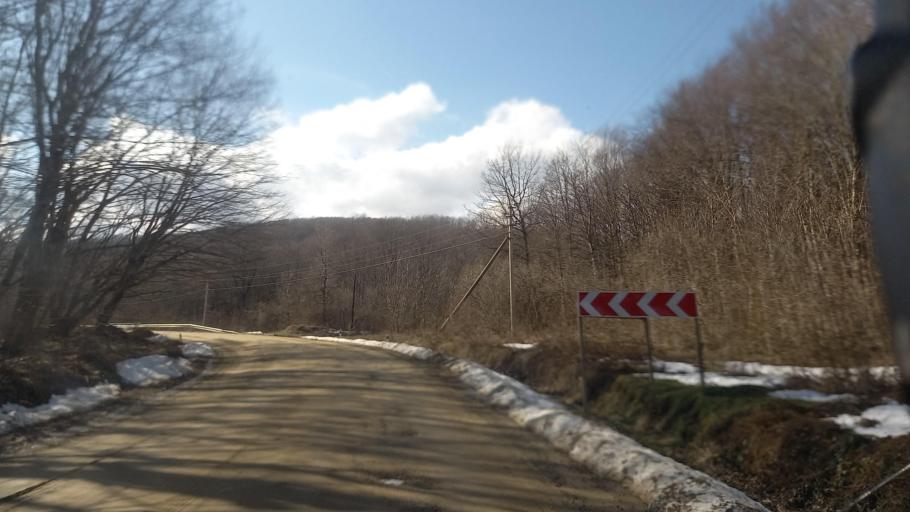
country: RU
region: Krasnodarskiy
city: Smolenskaya
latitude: 44.6574
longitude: 38.7319
